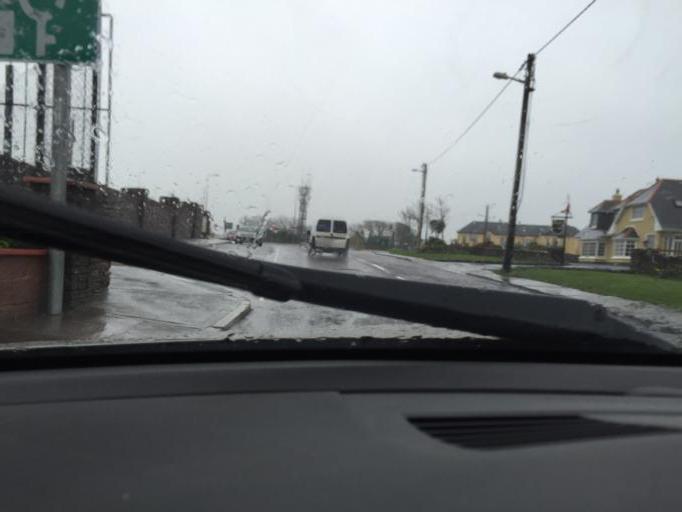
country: IE
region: Munster
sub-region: Ciarrai
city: Dingle
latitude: 52.1372
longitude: -10.2693
